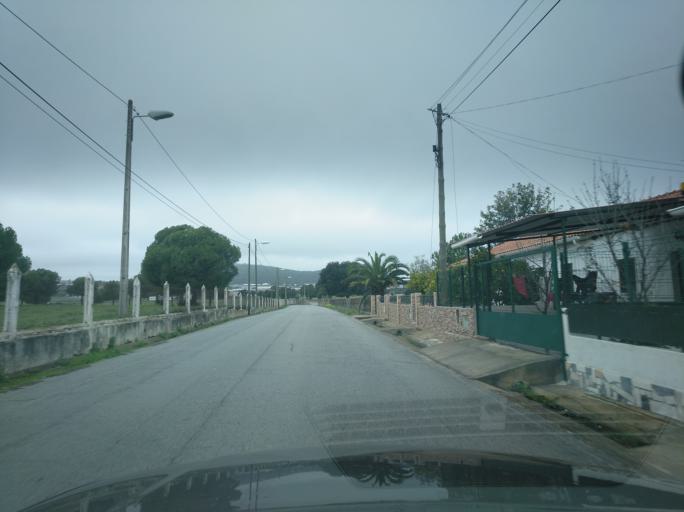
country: PT
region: Portalegre
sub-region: Elvas
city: Elvas
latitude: 38.8884
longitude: -7.1311
